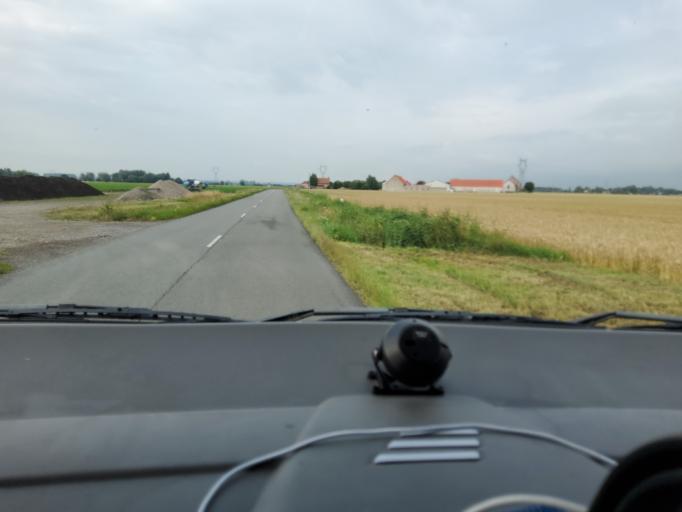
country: FR
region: Nord-Pas-de-Calais
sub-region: Departement du Nord
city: Bourbourg
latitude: 50.9314
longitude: 2.1921
